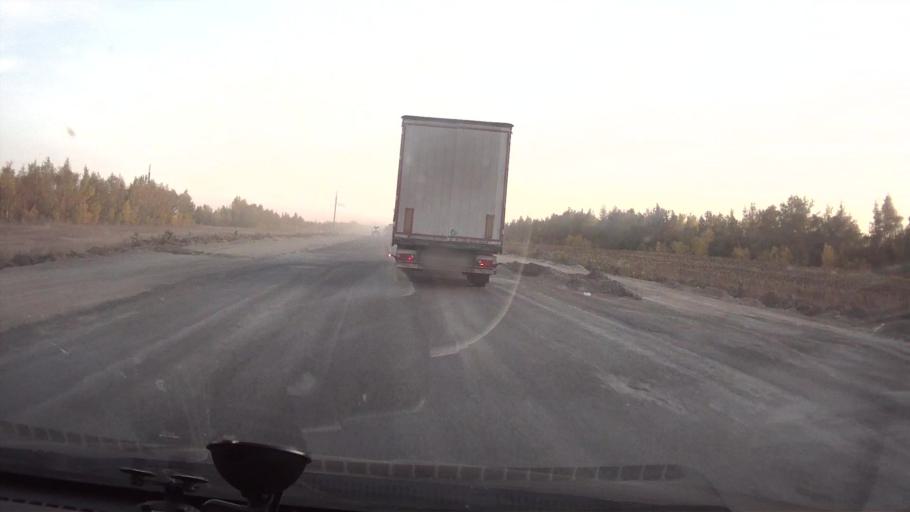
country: RU
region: Saratov
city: Kamenskiy
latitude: 50.9255
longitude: 45.5990
